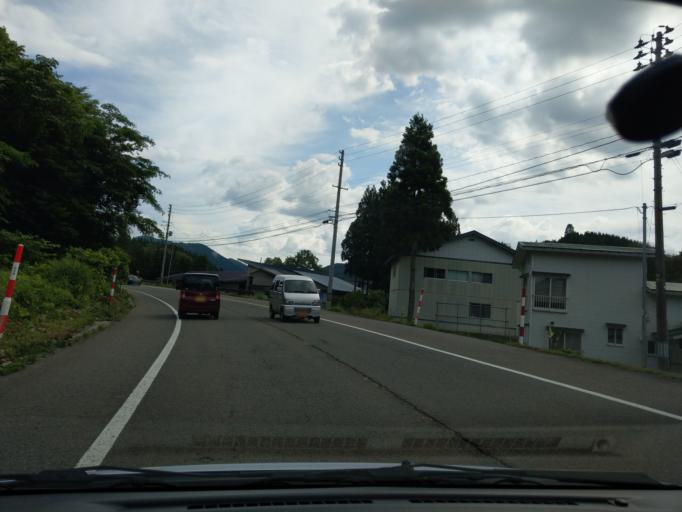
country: JP
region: Akita
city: Kakunodatemachi
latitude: 39.6949
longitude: 140.5735
